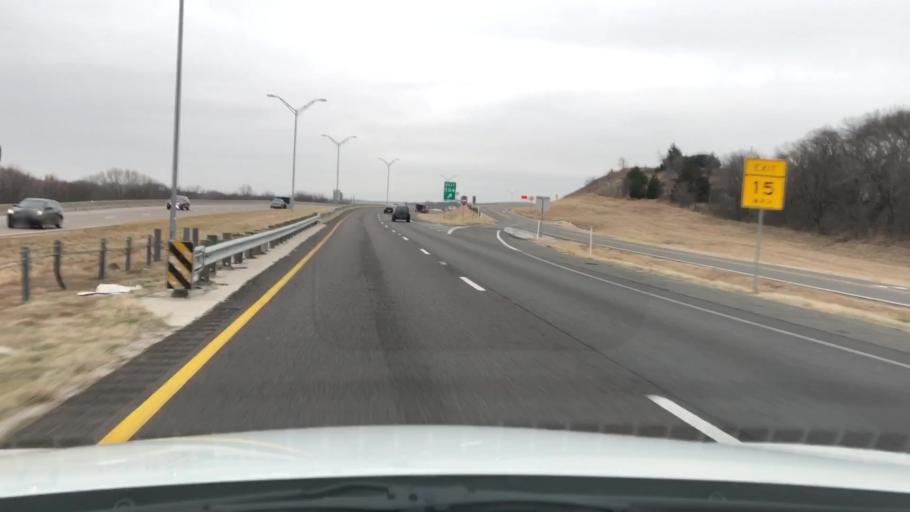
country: US
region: Texas
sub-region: Cooke County
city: Gainesville
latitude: 33.7223
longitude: -97.1613
